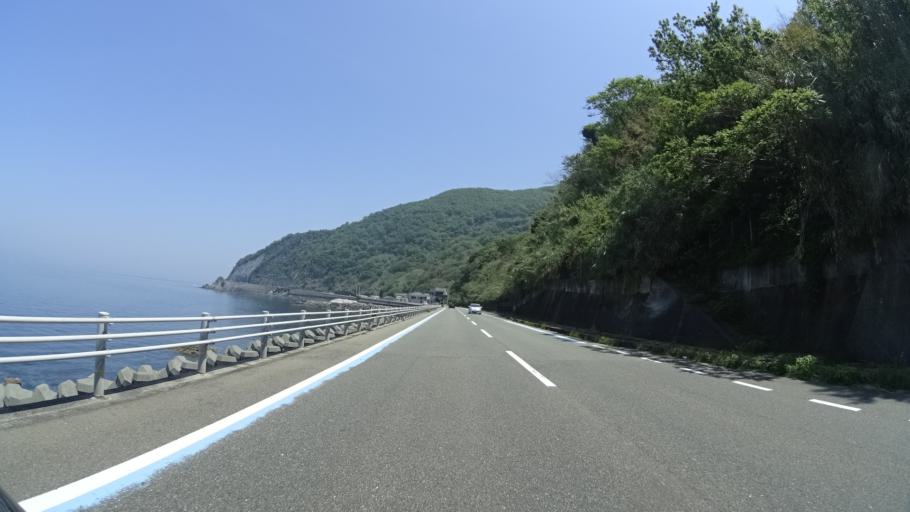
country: JP
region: Ehime
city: Ozu
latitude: 33.5872
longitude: 132.4545
